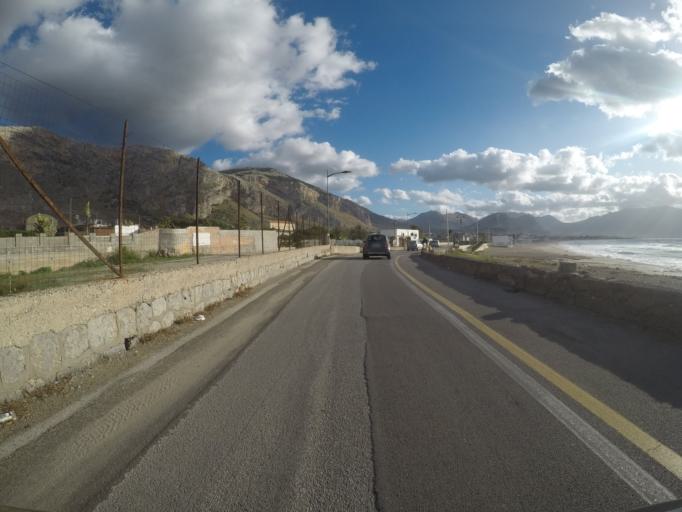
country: IT
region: Sicily
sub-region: Palermo
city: Isola delle Femmine
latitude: 38.1929
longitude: 13.2443
